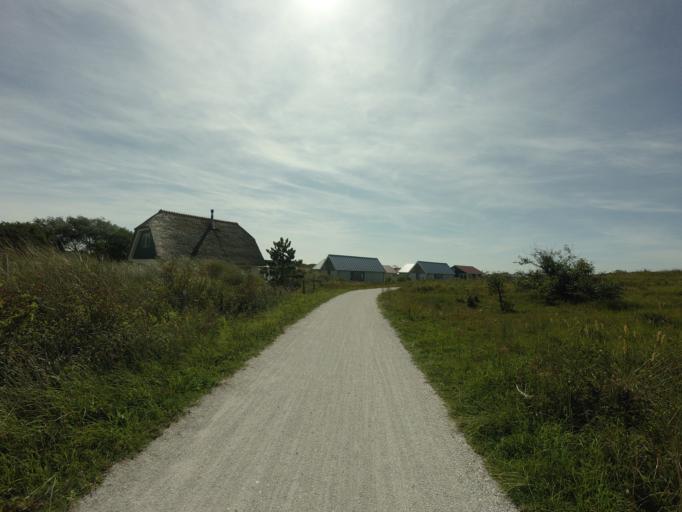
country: NL
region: Friesland
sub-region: Gemeente Ameland
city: Hollum
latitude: 53.4521
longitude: 5.6357
